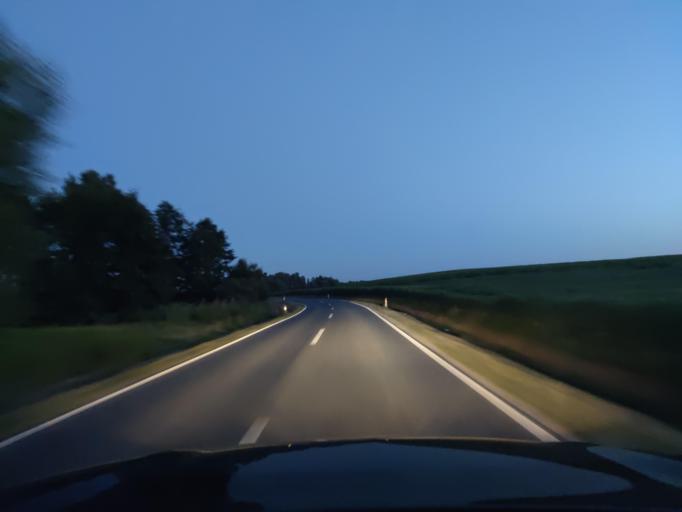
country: HR
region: Medimurska
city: Vratisinec
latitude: 46.4897
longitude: 16.4256
